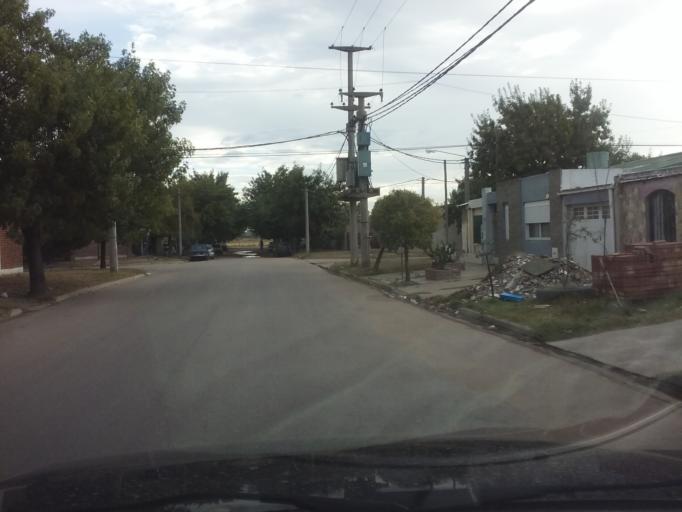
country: AR
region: La Pampa
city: Santa Rosa
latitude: -36.6485
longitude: -64.2947
